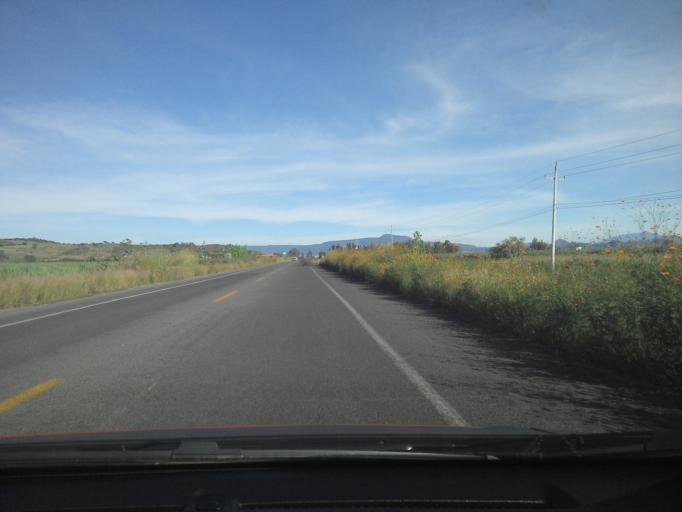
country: MX
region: Jalisco
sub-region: Teuchitlan
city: La Estanzuela
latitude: 20.6696
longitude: -103.8040
